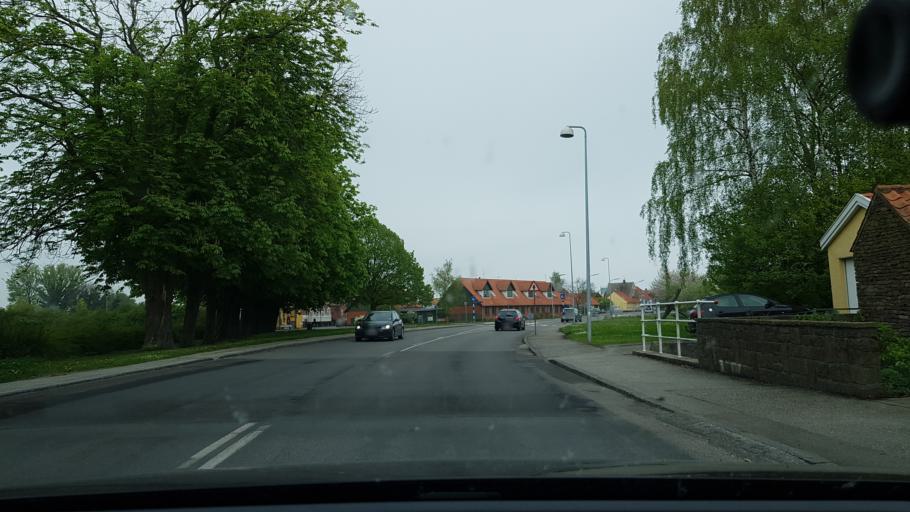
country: DK
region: Capital Region
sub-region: Bornholm Kommune
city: Nexo
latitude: 55.0567
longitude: 15.1271
